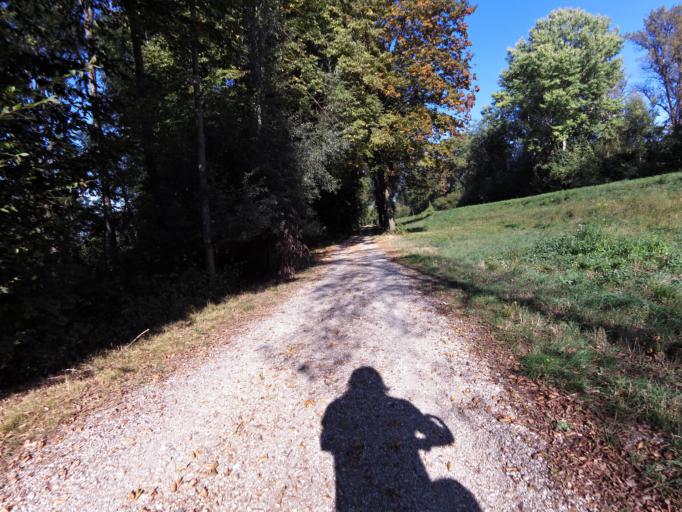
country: DE
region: Bavaria
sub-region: Lower Bavaria
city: Essenbach
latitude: 48.5905
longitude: 12.2382
